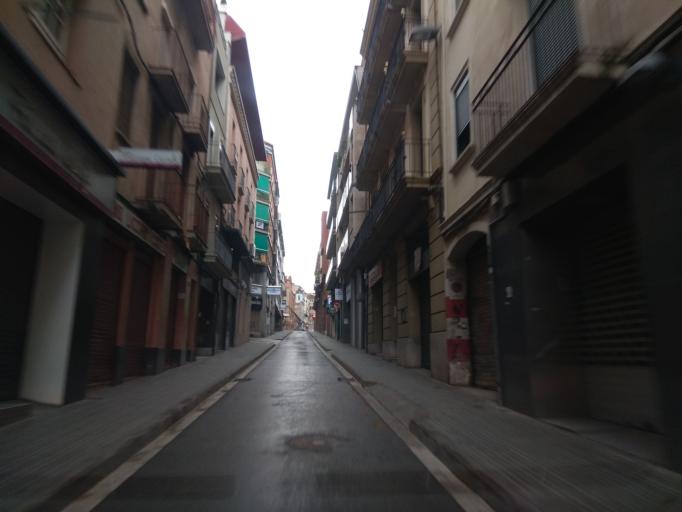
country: ES
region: Catalonia
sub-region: Provincia de Barcelona
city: Manresa
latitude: 41.7266
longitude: 1.8251
